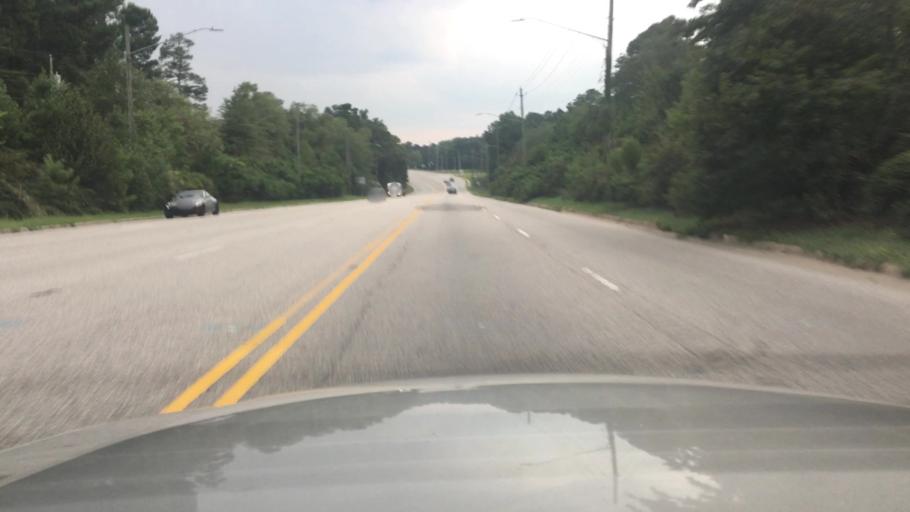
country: US
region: North Carolina
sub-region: Cumberland County
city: Fort Bragg
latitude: 35.1025
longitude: -78.9602
